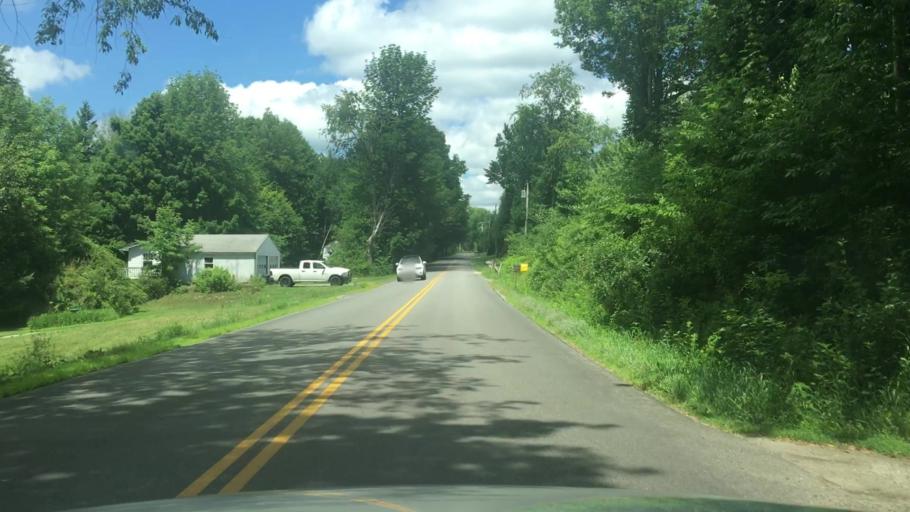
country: US
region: Maine
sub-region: Waldo County
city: Belfast
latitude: 44.4143
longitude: -69.0402
